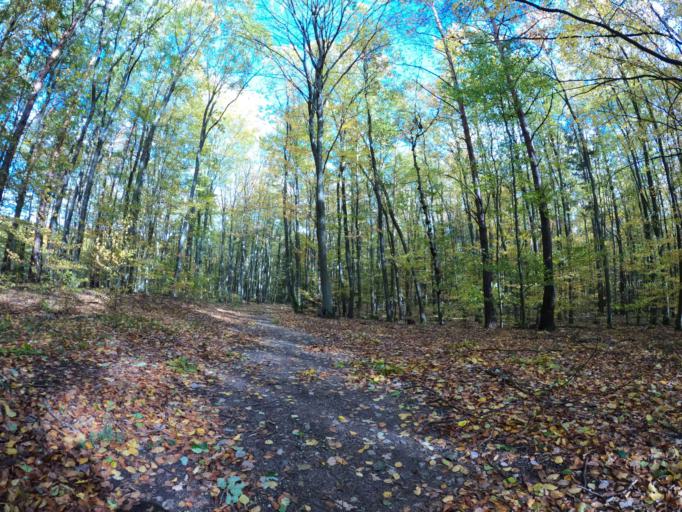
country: PL
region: West Pomeranian Voivodeship
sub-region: Powiat mysliborski
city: Barlinek
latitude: 52.9701
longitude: 15.2340
